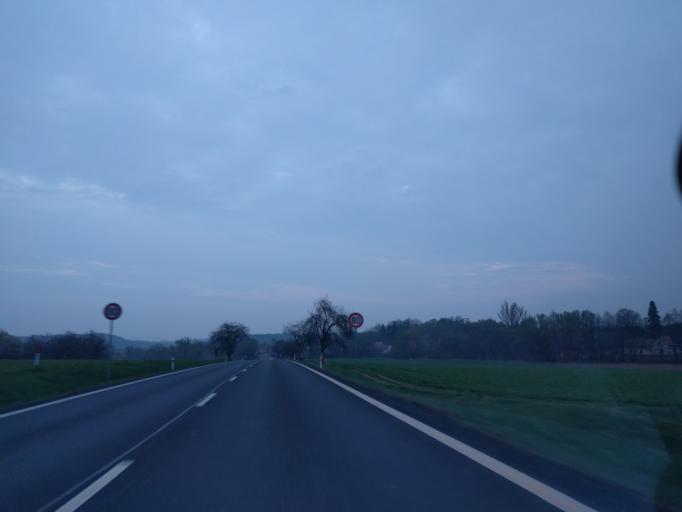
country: CZ
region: Central Bohemia
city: Jesenice
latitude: 50.1534
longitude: 13.5202
